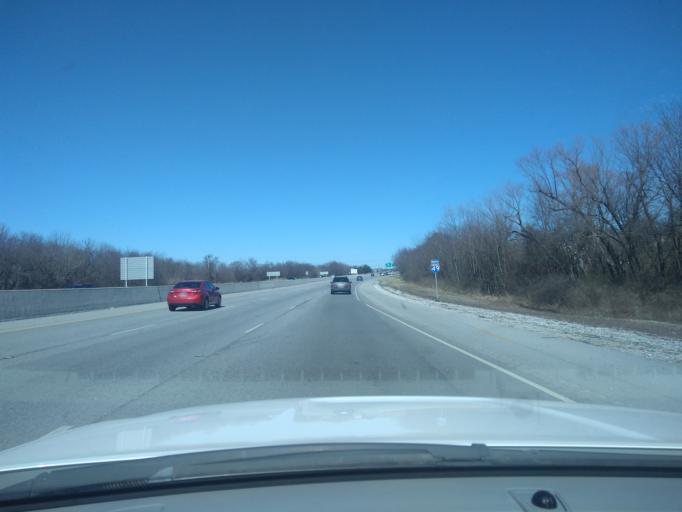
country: US
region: Arkansas
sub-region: Washington County
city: Fayetteville
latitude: 36.0833
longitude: -94.1979
